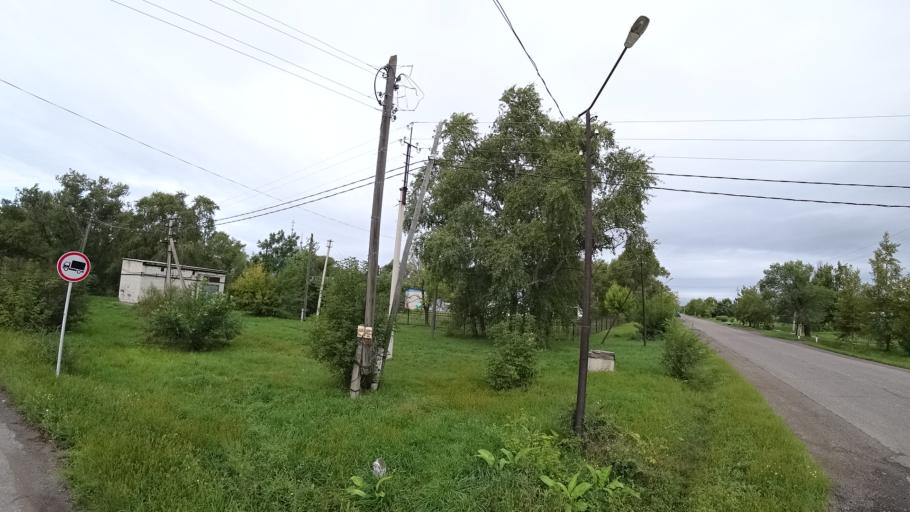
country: RU
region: Primorskiy
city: Chernigovka
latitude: 44.3410
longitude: 132.5833
